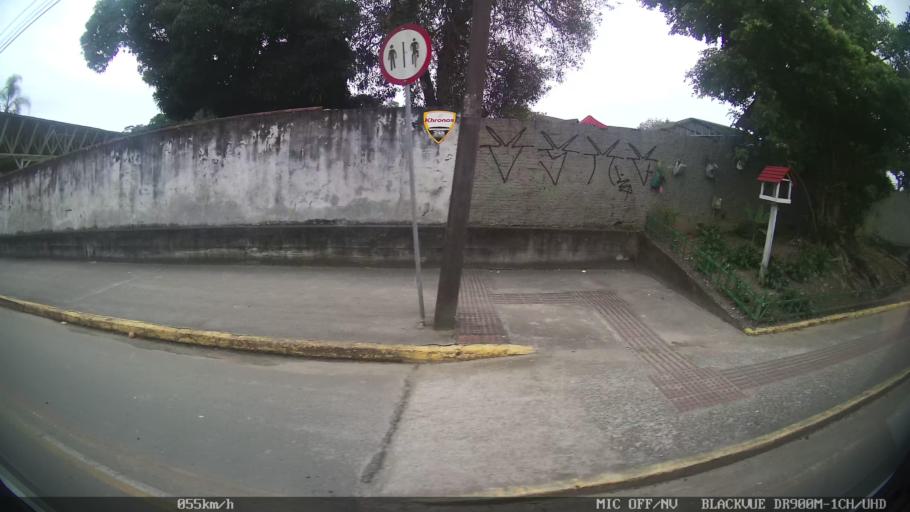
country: BR
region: Santa Catarina
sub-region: Joinville
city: Joinville
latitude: -26.2630
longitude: -48.8185
